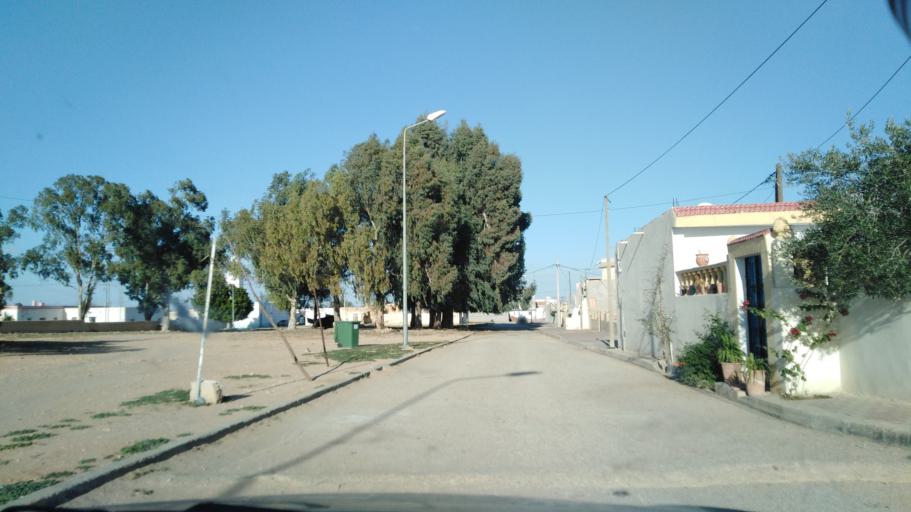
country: TN
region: Al Mahdiyah
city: Shurban
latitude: 34.9600
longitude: 10.3631
